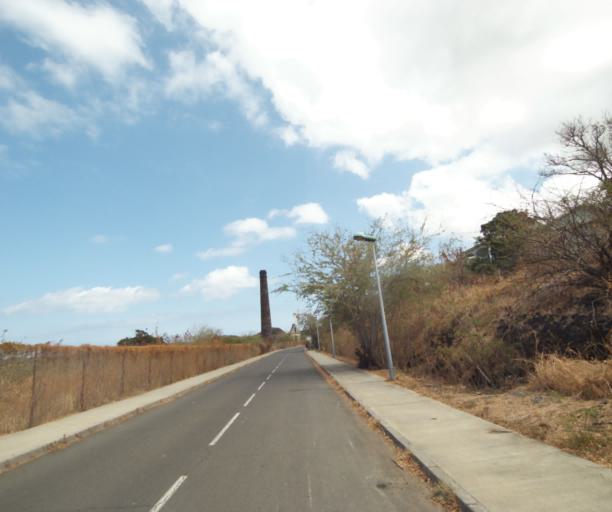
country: RE
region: Reunion
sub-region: Reunion
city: Trois-Bassins
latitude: -21.0839
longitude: 55.2374
